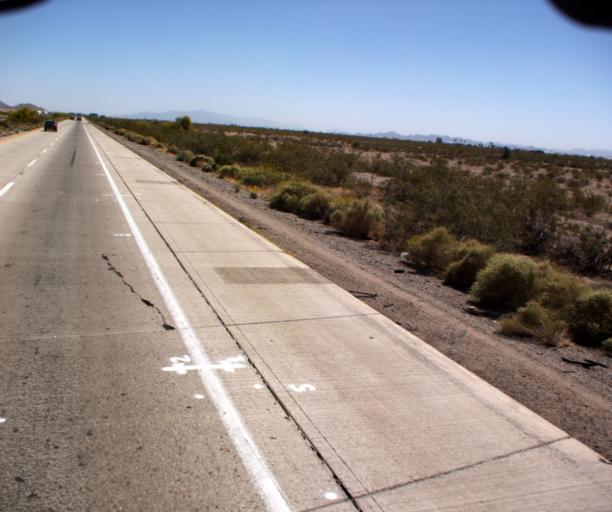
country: US
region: Arizona
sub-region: Maricopa County
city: Buckeye
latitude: 33.4458
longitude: -112.7072
